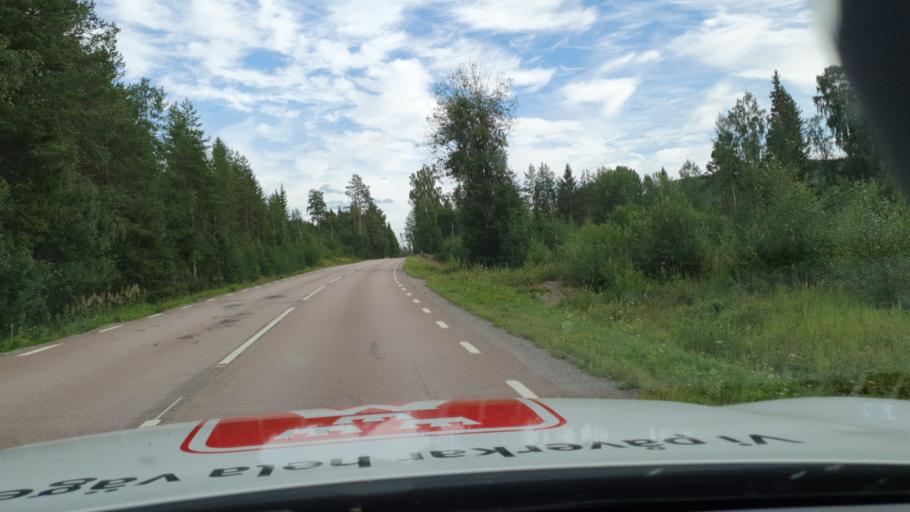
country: SE
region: Vaesternorrland
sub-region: Solleftea Kommun
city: As
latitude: 63.5794
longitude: 16.3956
